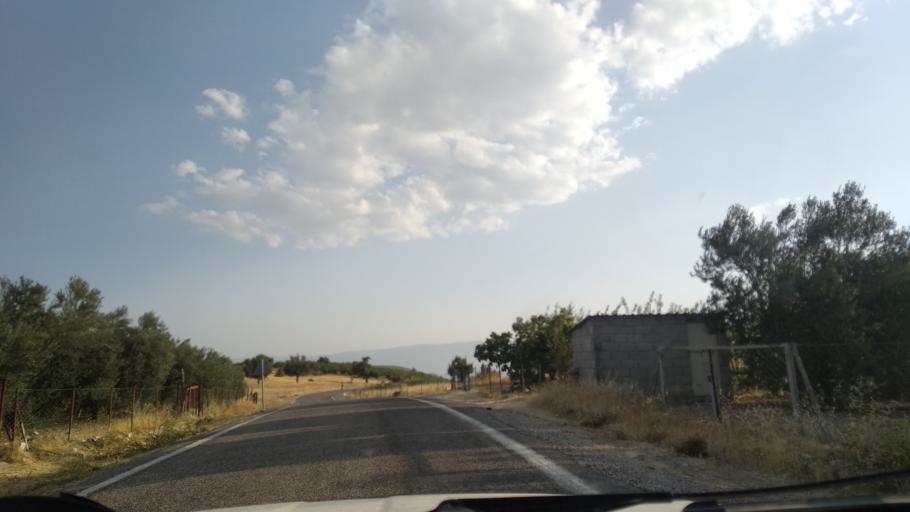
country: TR
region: Mersin
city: Sarikavak
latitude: 36.5650
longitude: 33.6333
